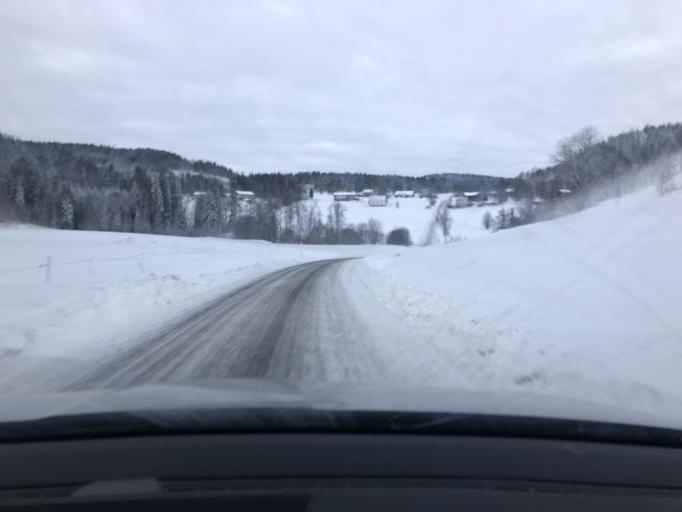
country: SE
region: Vaesternorrland
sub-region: Kramfors Kommun
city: Nordingra
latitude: 62.9103
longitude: 18.2368
